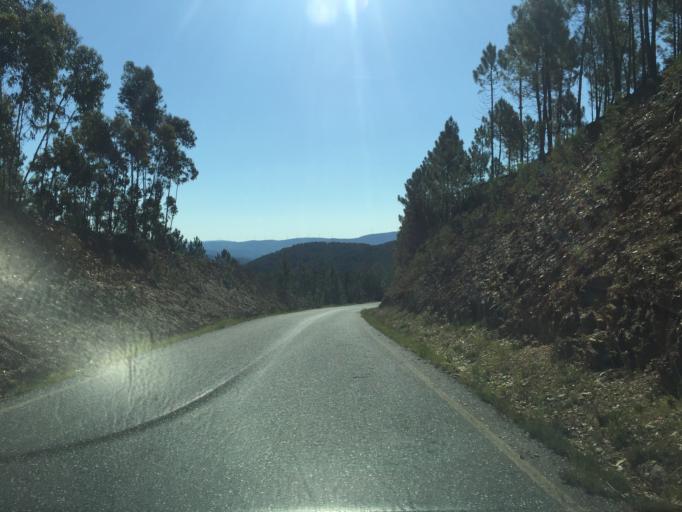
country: PT
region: Coimbra
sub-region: Pampilhosa da Serra
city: Pampilhosa da Serra
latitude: 40.0527
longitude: -7.8434
